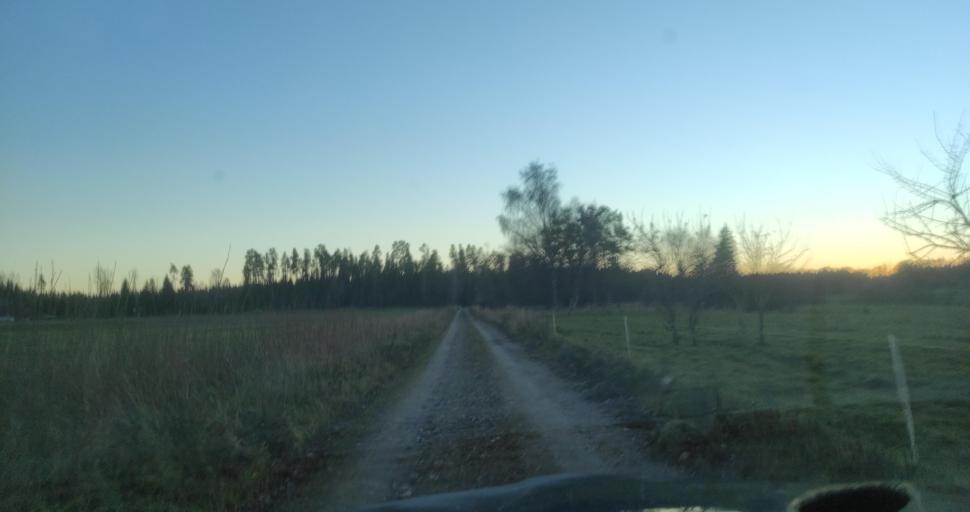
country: LV
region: Dundaga
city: Dundaga
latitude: 57.3726
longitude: 22.2253
